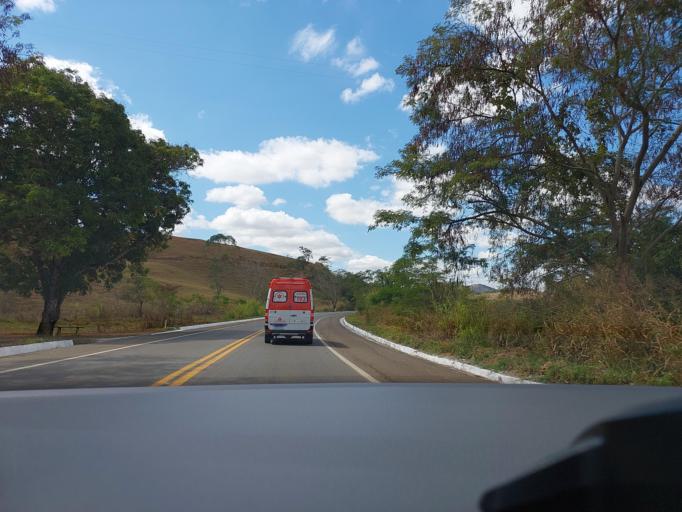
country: BR
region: Minas Gerais
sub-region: Muriae
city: Muriae
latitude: -21.1378
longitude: -42.3046
